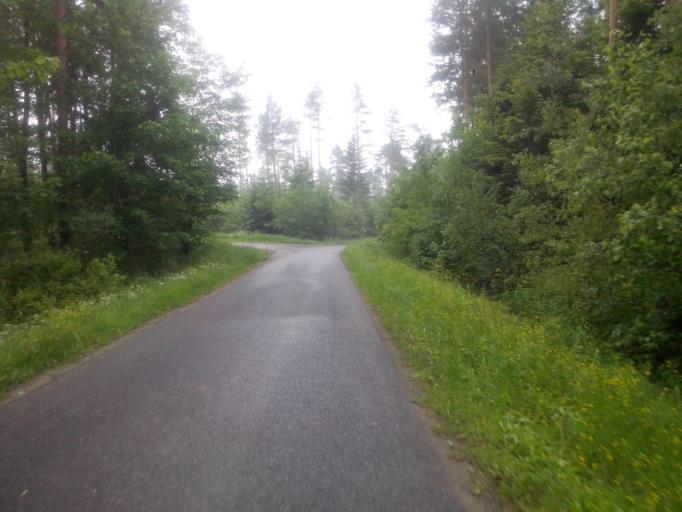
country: PL
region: Subcarpathian Voivodeship
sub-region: Powiat strzyzowski
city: Wysoka Strzyzowska
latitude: 49.8154
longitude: 21.7876
